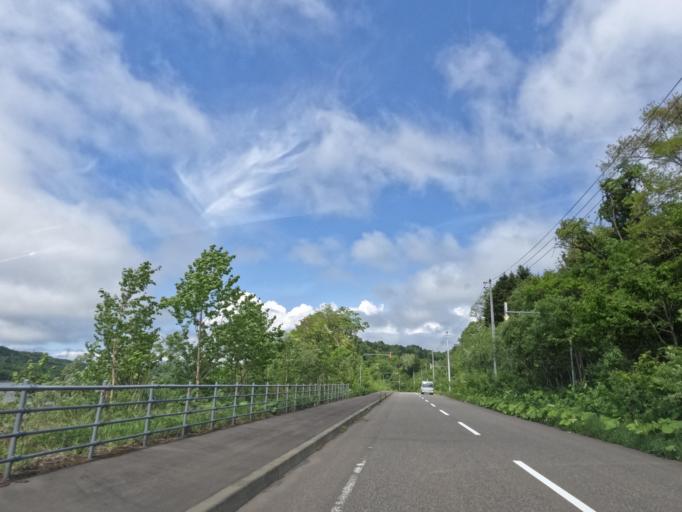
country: JP
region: Hokkaido
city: Tobetsu
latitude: 43.3517
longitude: 141.5685
